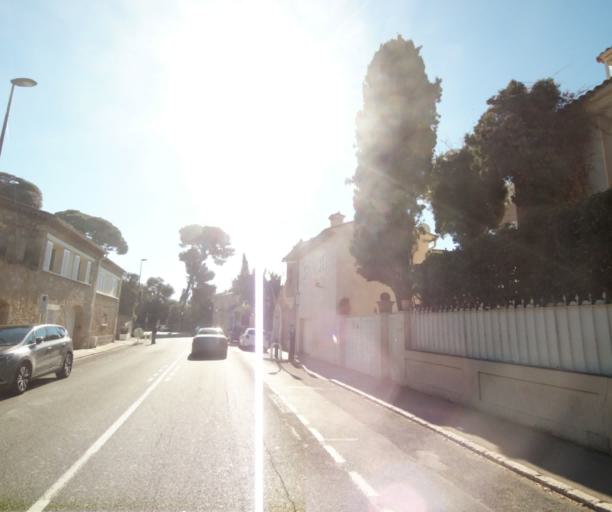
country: FR
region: Provence-Alpes-Cote d'Azur
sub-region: Departement des Alpes-Maritimes
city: Antibes
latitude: 43.5646
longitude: 7.1157
